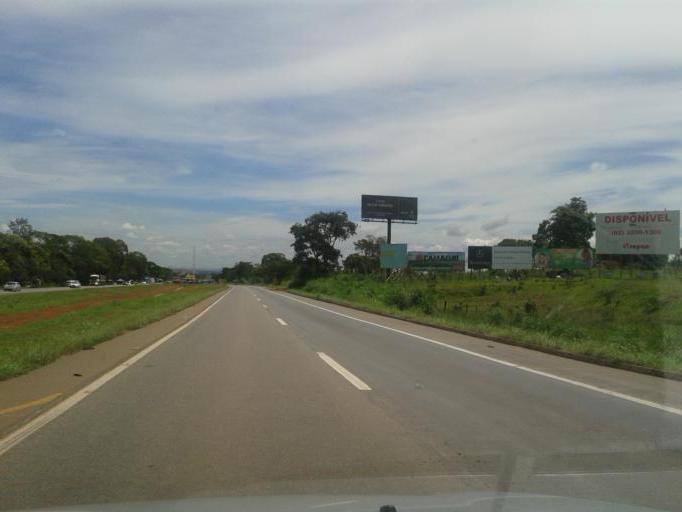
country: BR
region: Goias
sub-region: Hidrolandia
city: Hidrolandia
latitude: -16.9289
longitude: -49.2515
